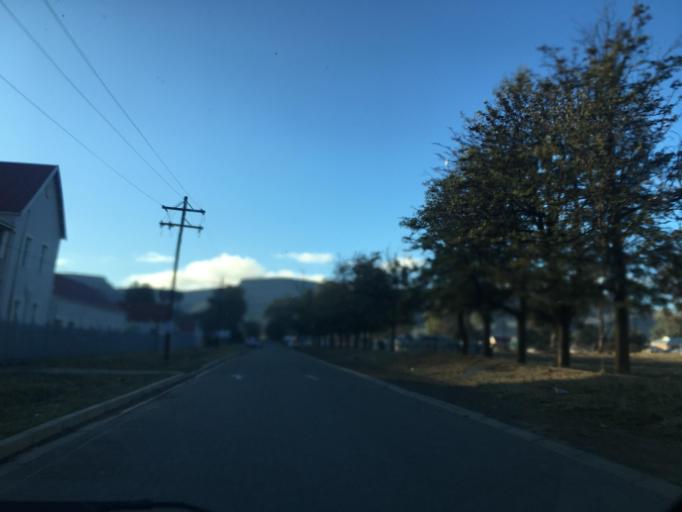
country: ZA
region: Eastern Cape
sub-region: Chris Hani District Municipality
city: Cala
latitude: -31.5256
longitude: 27.6983
